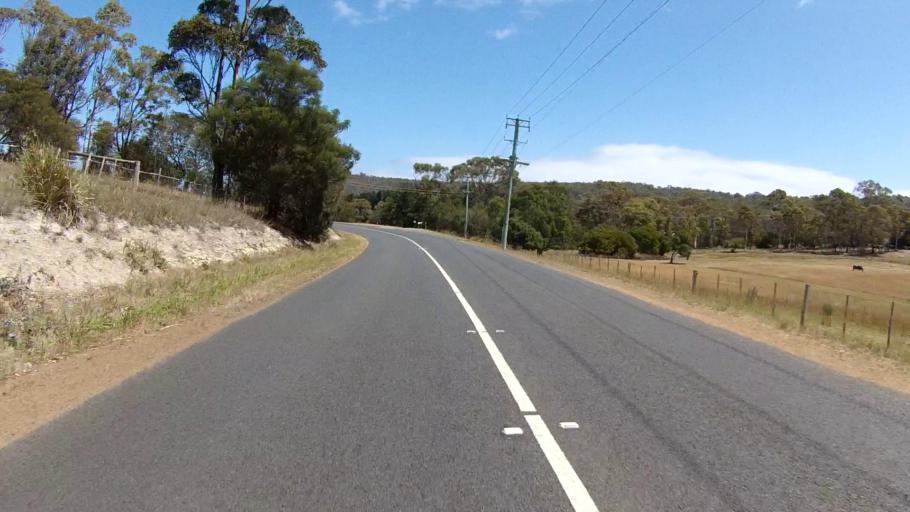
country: AU
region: Tasmania
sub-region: Clarence
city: Sandford
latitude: -42.9569
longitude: 147.4762
